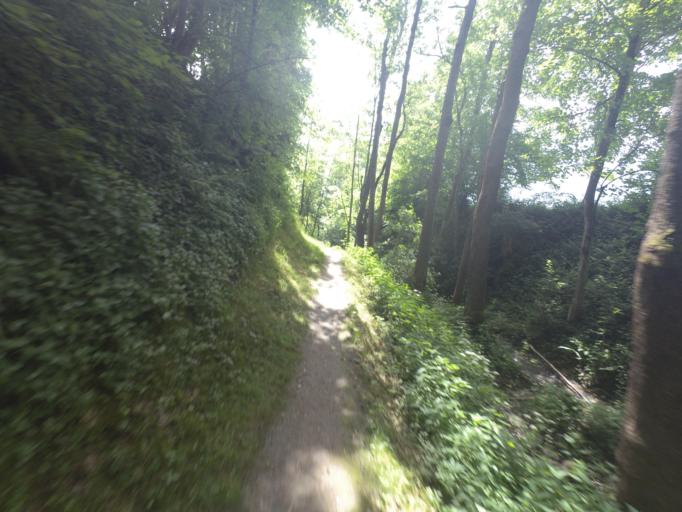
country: AT
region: Salzburg
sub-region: Politischer Bezirk Sankt Johann im Pongau
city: Sankt Veit im Pongau
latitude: 47.3298
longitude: 13.1398
